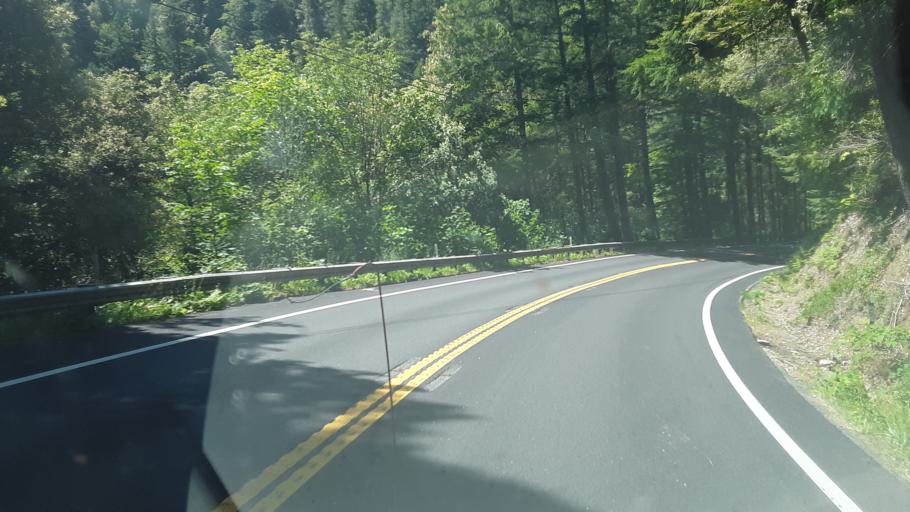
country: US
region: California
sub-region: Del Norte County
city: Bertsch-Oceanview
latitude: 41.8231
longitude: -124.0317
